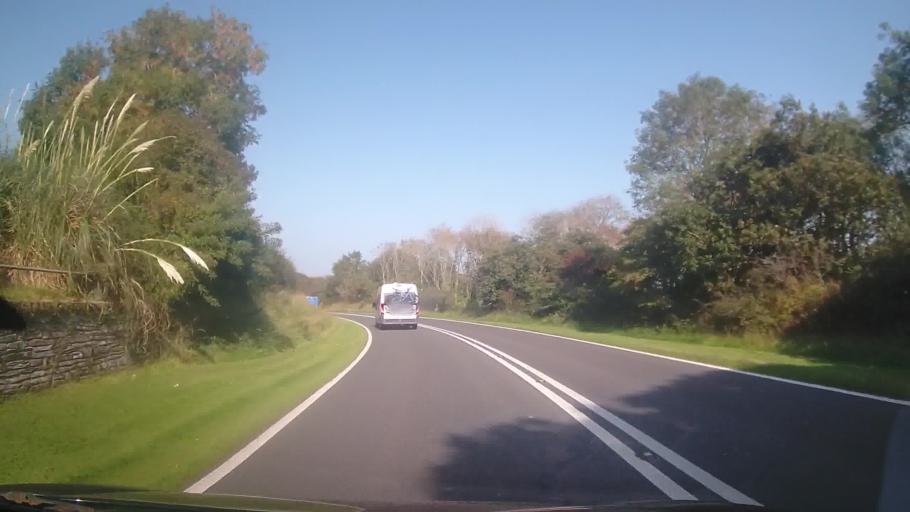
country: GB
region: Wales
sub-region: County of Ceredigion
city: Cardigan
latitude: 52.0726
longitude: -4.6587
